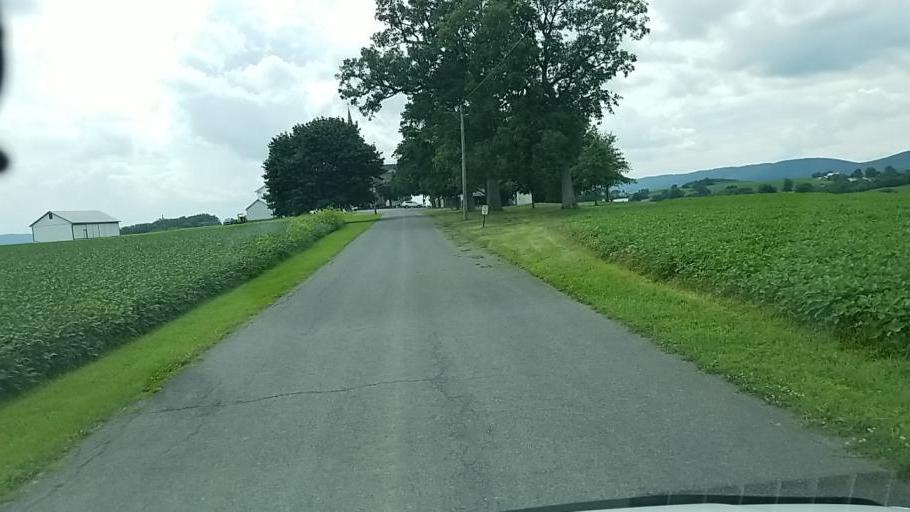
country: US
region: Pennsylvania
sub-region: Dauphin County
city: Elizabethville
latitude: 40.5878
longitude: -76.8144
